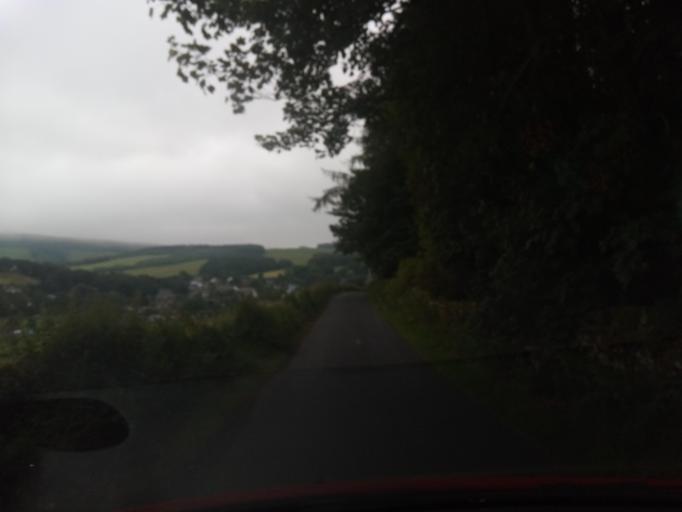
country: GB
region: Scotland
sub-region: The Scottish Borders
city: Galashiels
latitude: 55.6940
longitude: -2.8700
